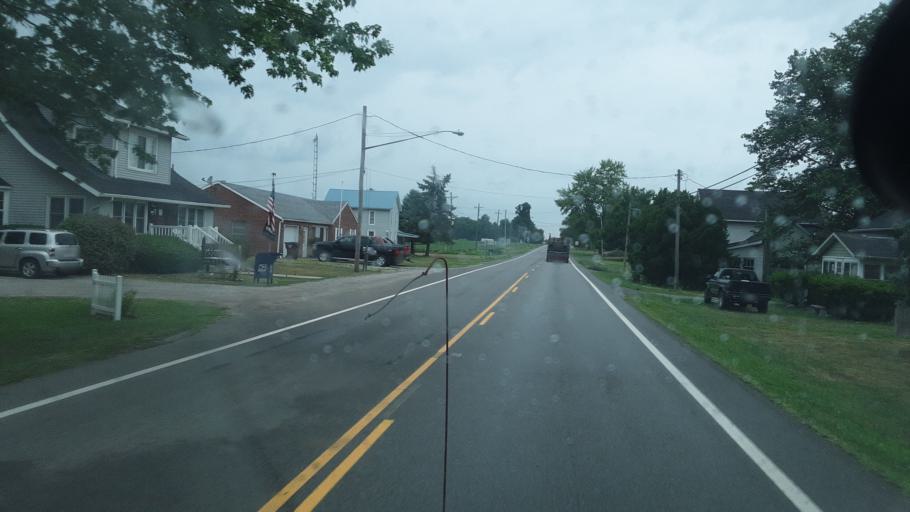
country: US
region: Ohio
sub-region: Williams County
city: Bryan
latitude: 41.3838
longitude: -84.6311
